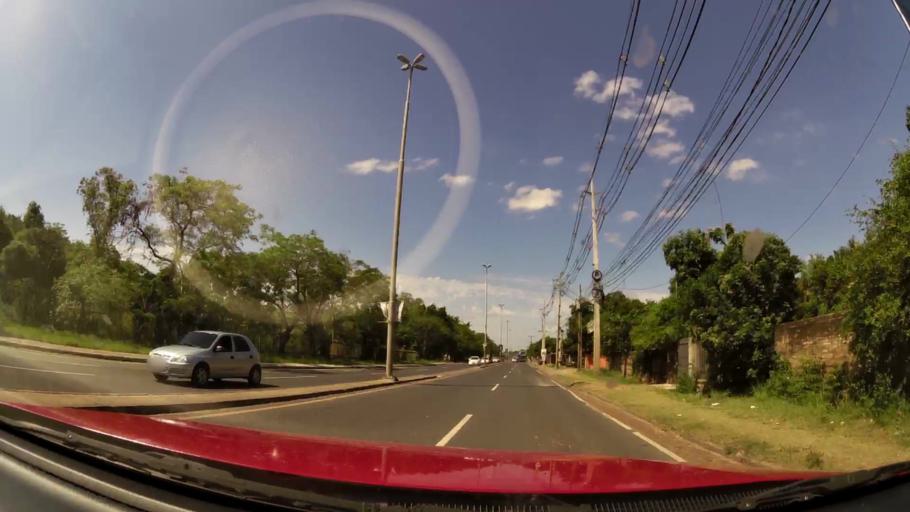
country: PY
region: Asuncion
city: Asuncion
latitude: -25.2555
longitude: -57.5644
